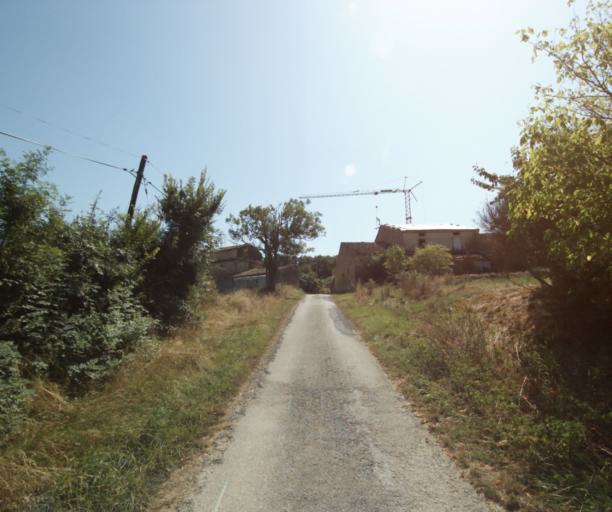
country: FR
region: Midi-Pyrenees
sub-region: Departement de la Haute-Garonne
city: Saint-Felix-Lauragais
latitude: 43.4519
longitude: 1.8689
